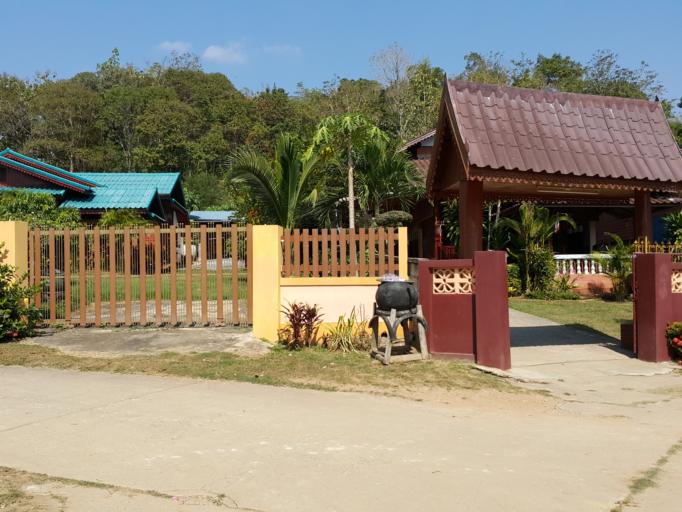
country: TH
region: Sukhothai
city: Thung Saliam
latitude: 17.3319
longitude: 99.4587
